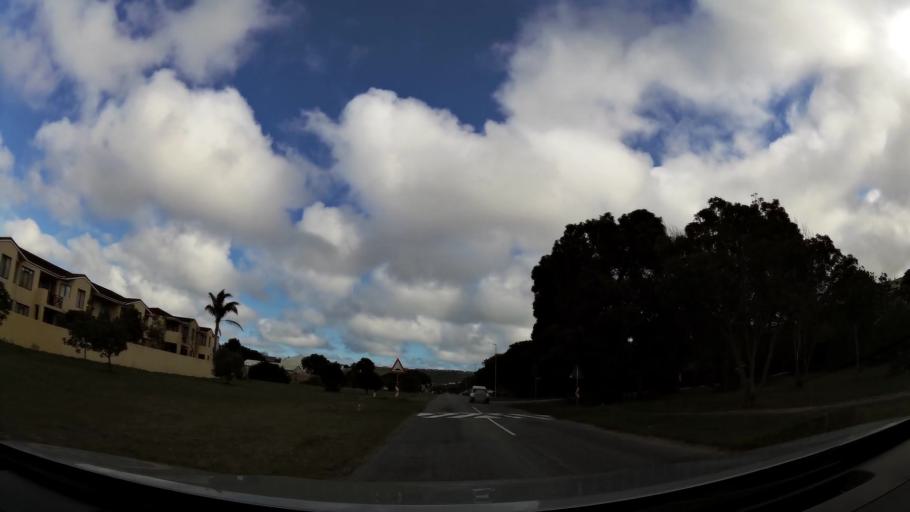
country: ZA
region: Western Cape
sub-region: Eden District Municipality
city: Plettenberg Bay
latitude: -34.0729
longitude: 23.3673
